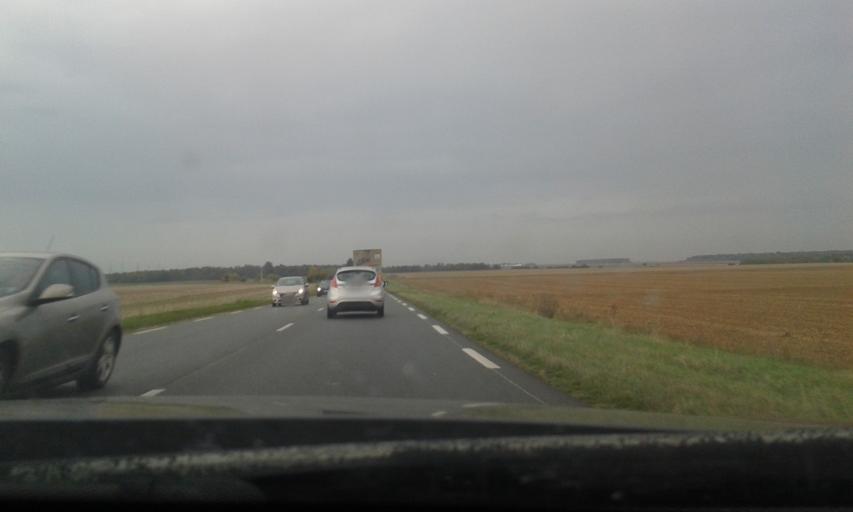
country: FR
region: Centre
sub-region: Departement d'Eure-et-Loir
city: Janville
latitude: 48.2196
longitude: 1.8058
